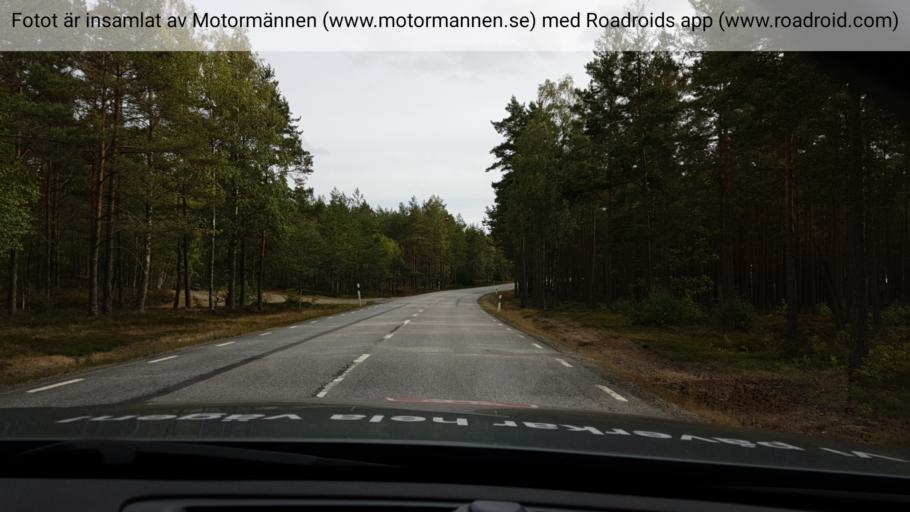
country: SE
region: Stockholm
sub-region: Botkyrka Kommun
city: Varsta
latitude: 59.0804
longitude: 17.7867
